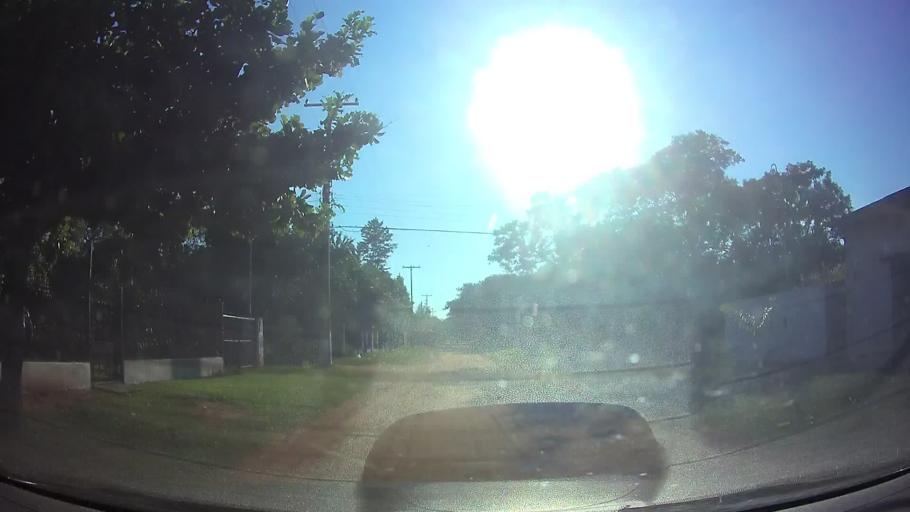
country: PY
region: Central
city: San Lorenzo
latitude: -25.2571
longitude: -57.4693
